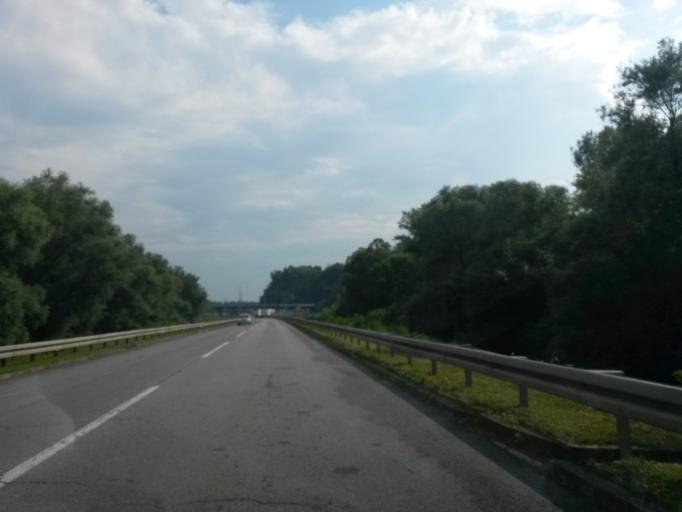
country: RS
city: Bogojevo
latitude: 45.5182
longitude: 19.0803
